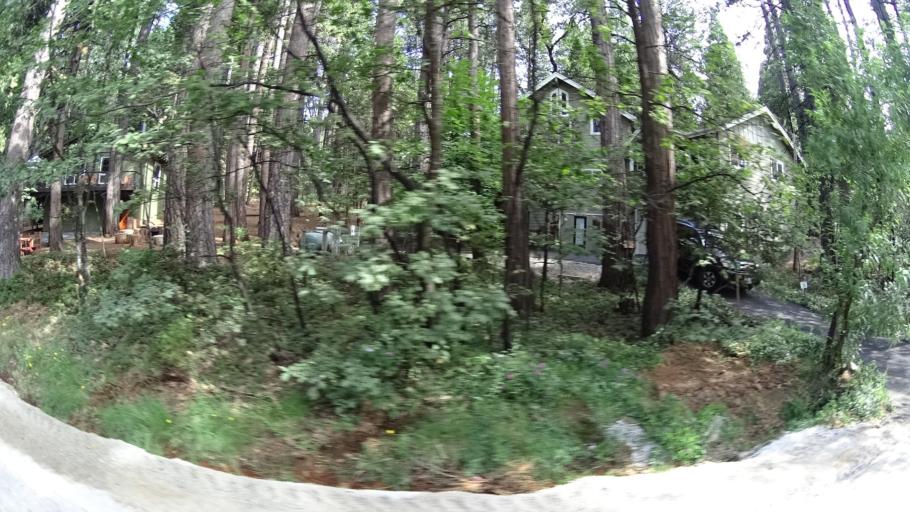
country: US
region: California
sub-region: Calaveras County
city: Arnold
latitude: 38.2543
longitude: -120.3320
